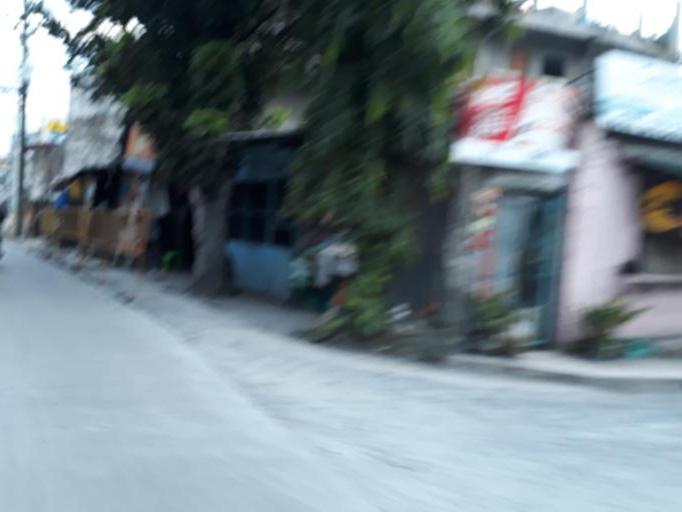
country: PH
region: Central Luzon
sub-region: Province of Bulacan
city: Meycauayan
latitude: 14.7261
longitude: 120.9888
